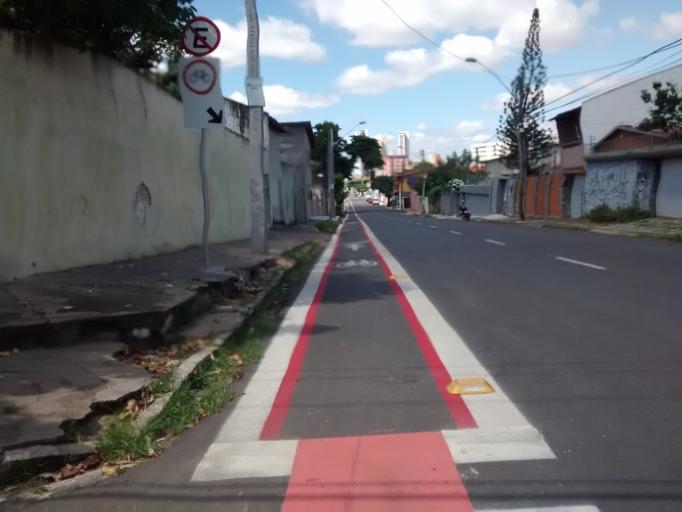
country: BR
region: Ceara
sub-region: Fortaleza
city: Fortaleza
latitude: -3.7281
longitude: -38.5608
